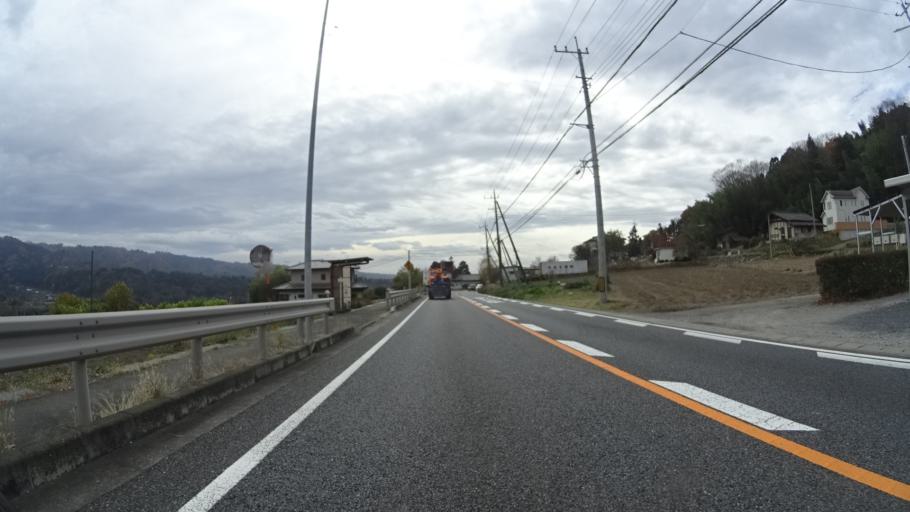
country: JP
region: Gunma
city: Numata
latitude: 36.5602
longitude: 139.0376
